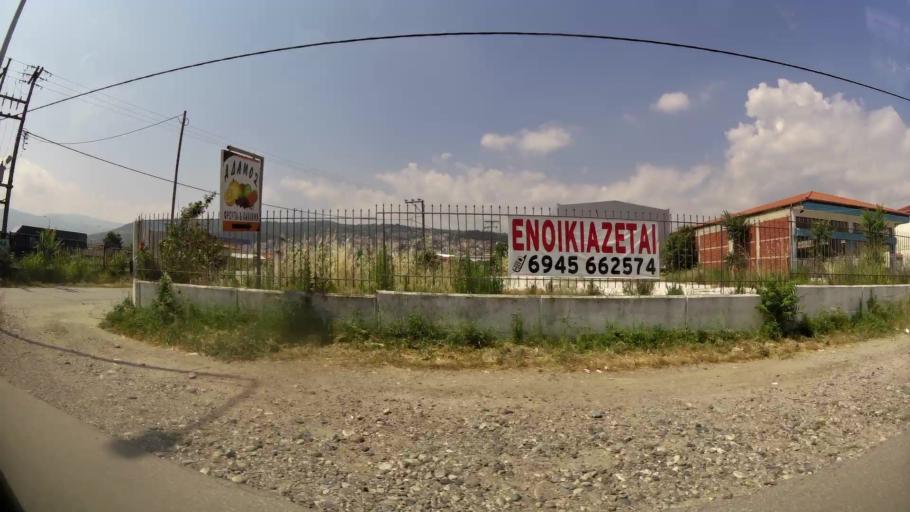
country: GR
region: Central Macedonia
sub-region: Nomos Imathias
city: Veroia
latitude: 40.5269
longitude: 22.2151
